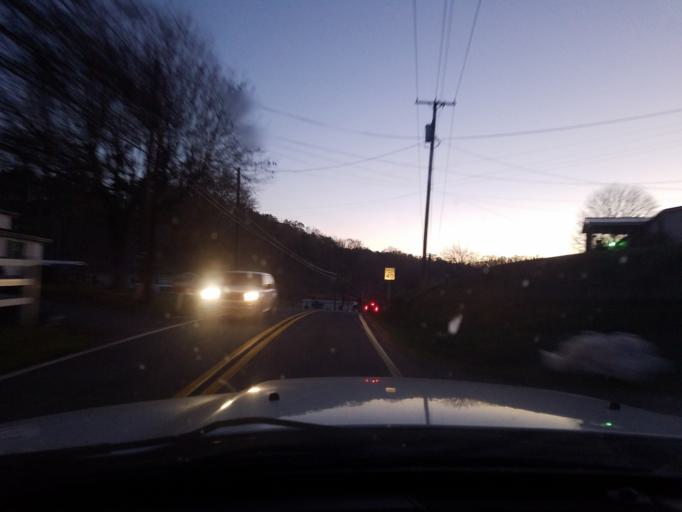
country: US
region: West Virginia
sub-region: Cabell County
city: Milton
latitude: 38.4604
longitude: -82.1089
